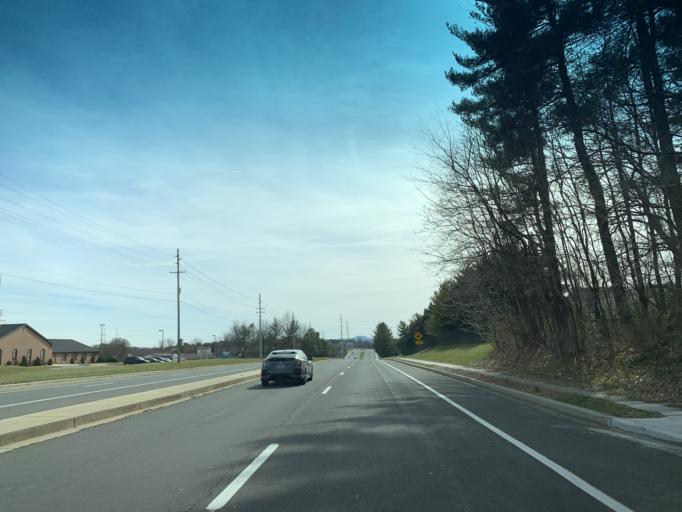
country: US
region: Maryland
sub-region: Frederick County
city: Ballenger Creek
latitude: 39.3880
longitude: -77.4227
